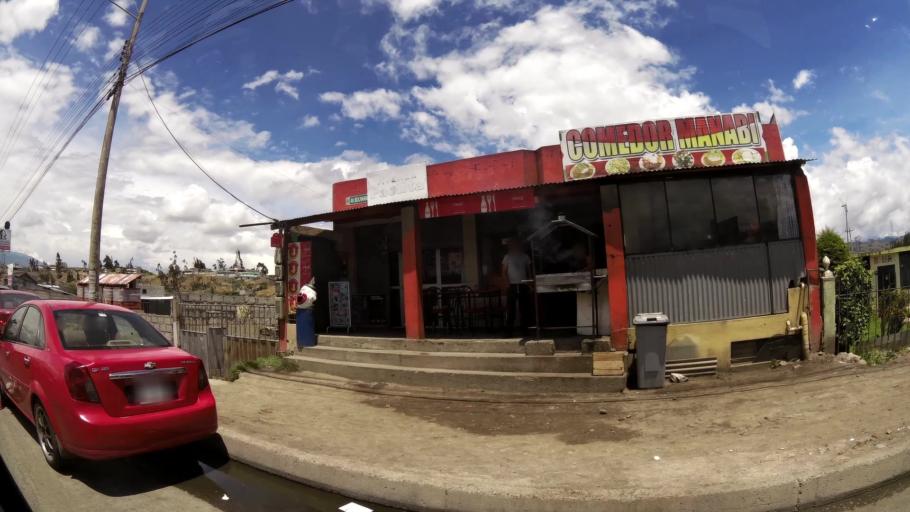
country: EC
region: Tungurahua
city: Ambato
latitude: -1.2868
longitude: -78.6070
